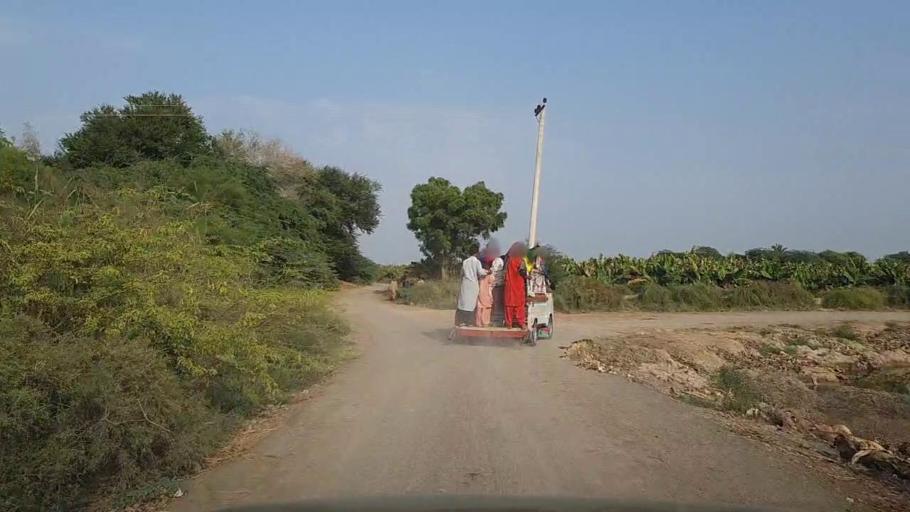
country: PK
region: Sindh
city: Thatta
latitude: 24.6437
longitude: 67.9482
